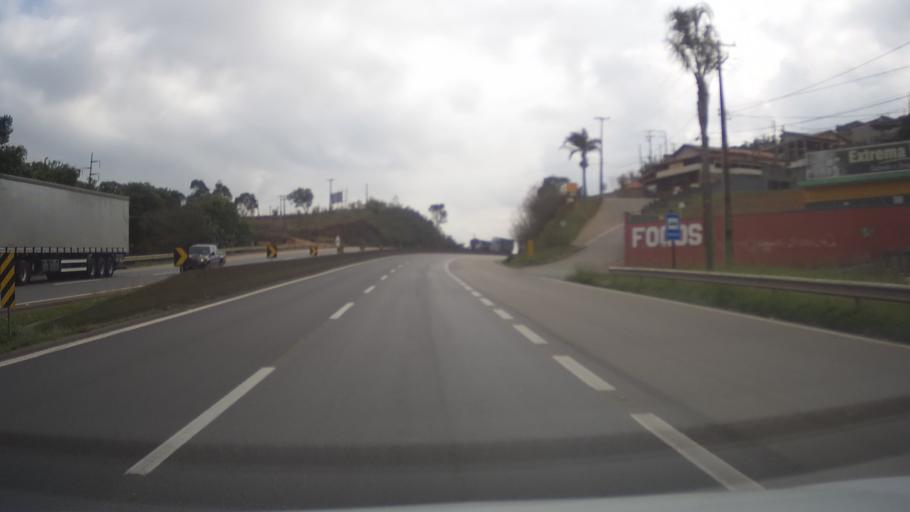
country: BR
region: Minas Gerais
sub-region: Extrema
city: Extrema
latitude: -22.8242
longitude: -46.3092
